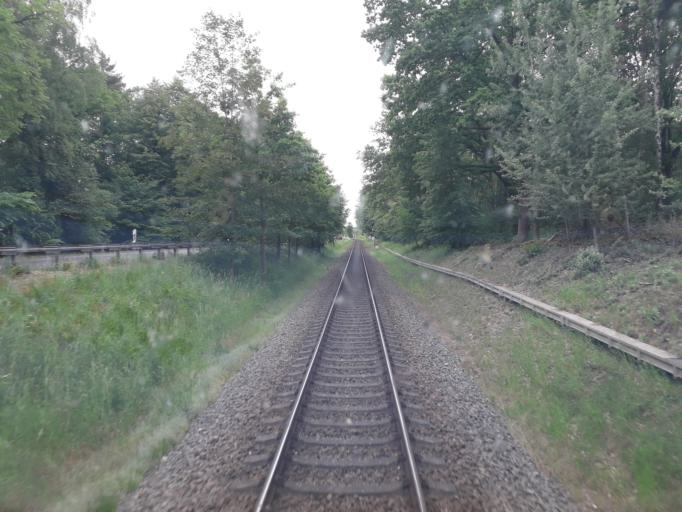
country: DE
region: Brandenburg
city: Neuruppin
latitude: 52.9237
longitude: 12.8302
